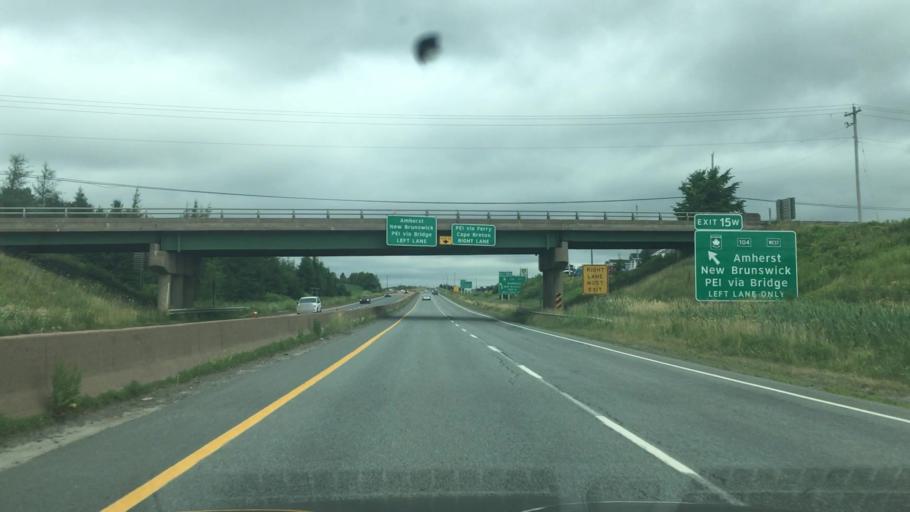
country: CA
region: Nova Scotia
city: Truro
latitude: 45.3805
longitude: -63.3209
